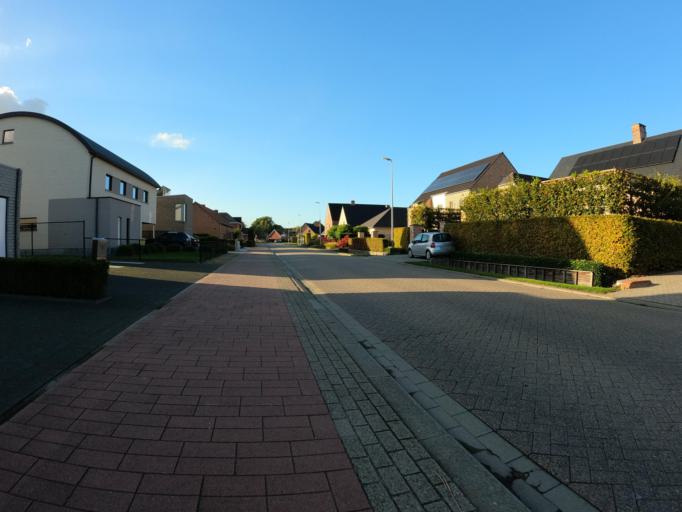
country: BE
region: Flanders
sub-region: Provincie Antwerpen
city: Heist-op-den-Berg
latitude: 51.0421
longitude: 4.7243
